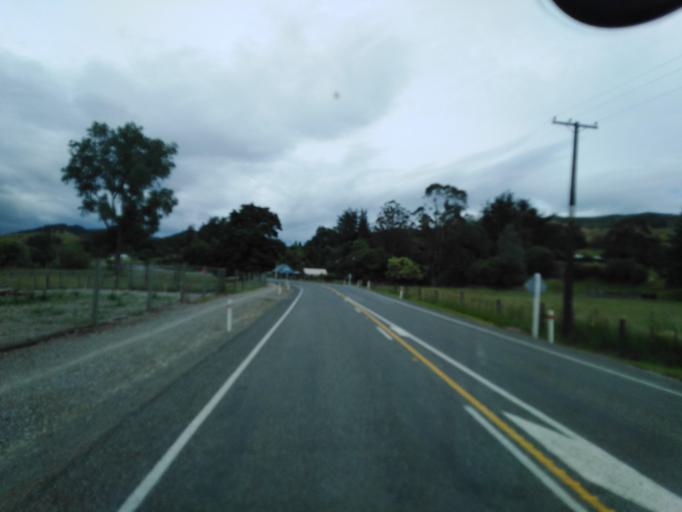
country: NZ
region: Tasman
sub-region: Tasman District
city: Wakefield
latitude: -41.4552
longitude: 172.9555
